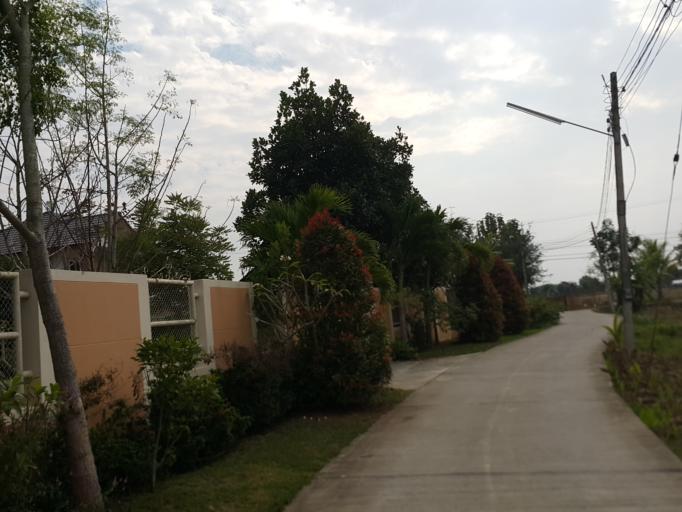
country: TH
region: Chiang Mai
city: San Kamphaeng
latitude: 18.8255
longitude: 99.1399
